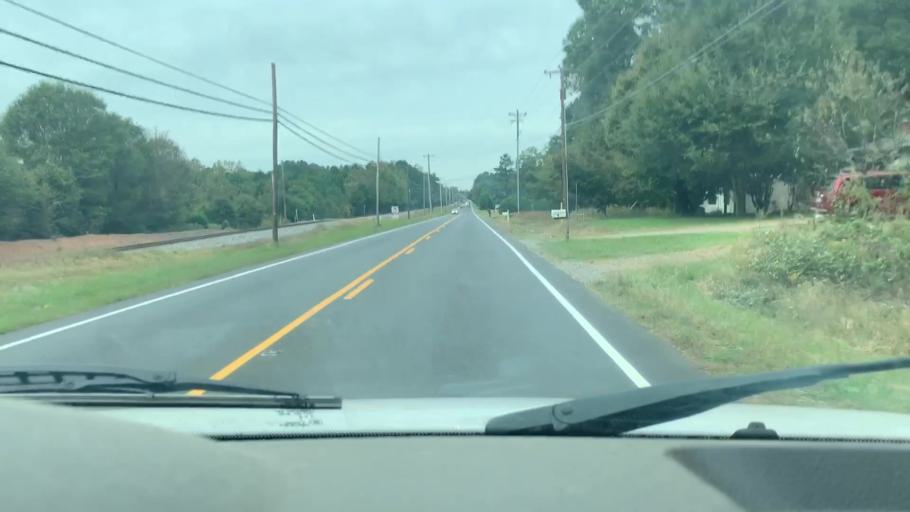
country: US
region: North Carolina
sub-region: Gaston County
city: Davidson
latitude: 35.5235
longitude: -80.8425
